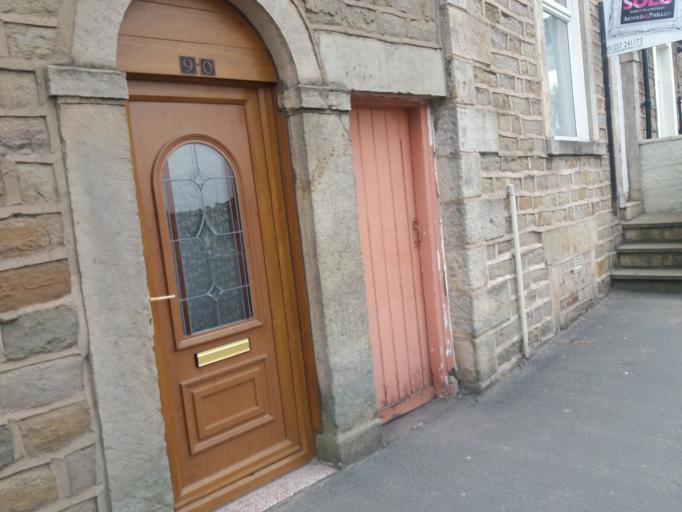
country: GB
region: England
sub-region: Lancashire
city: Chorley
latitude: 53.6526
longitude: -2.6178
